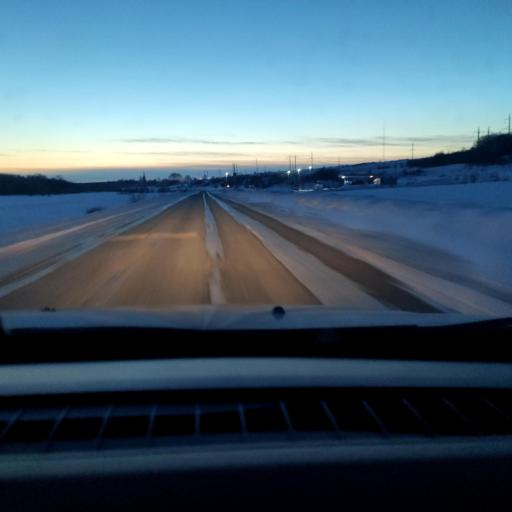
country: RU
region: Samara
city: Georgiyevka
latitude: 53.3227
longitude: 50.8771
